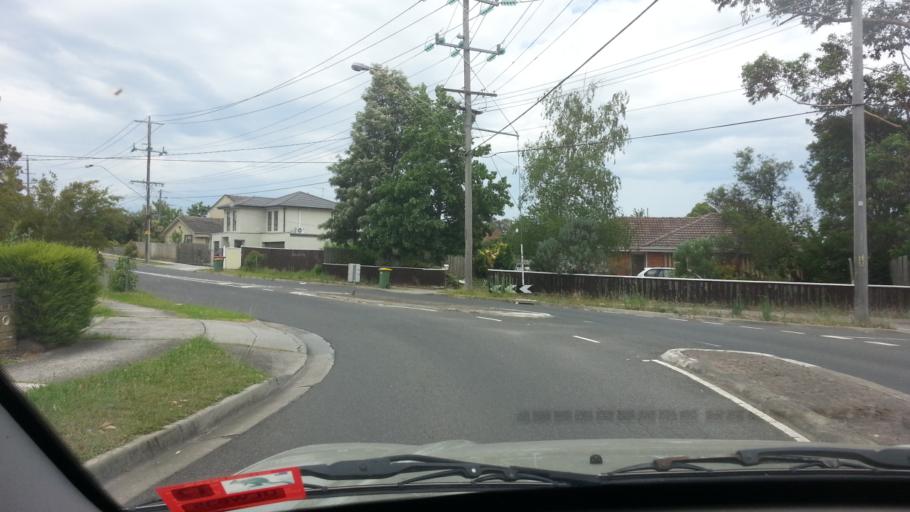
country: AU
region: Victoria
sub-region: Knox
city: Bayswater
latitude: -37.8603
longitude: 145.2516
